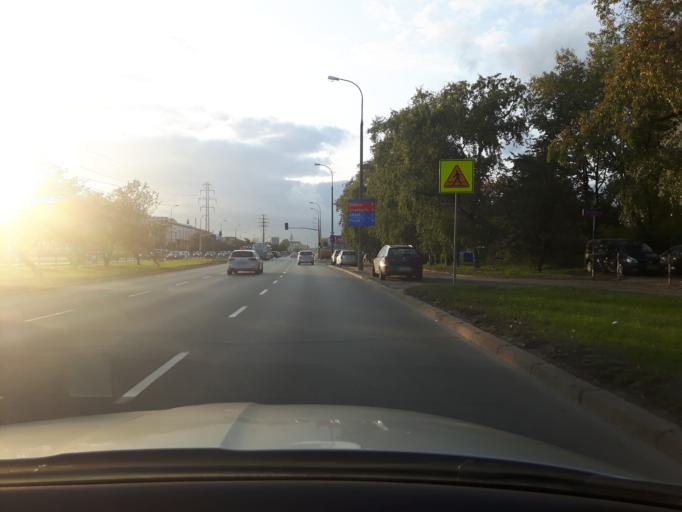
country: PL
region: Masovian Voivodeship
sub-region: Warszawa
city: Ursynow
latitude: 52.1509
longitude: 21.0288
